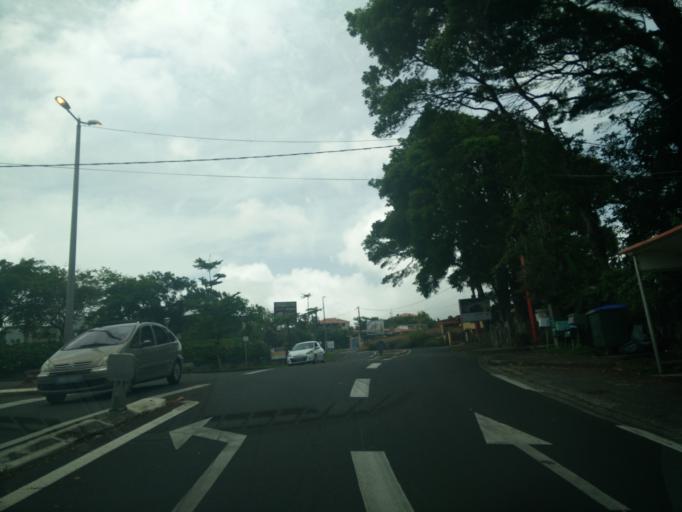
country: MQ
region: Martinique
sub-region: Martinique
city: Le Morne-Rouge
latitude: 14.7827
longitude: -61.1365
